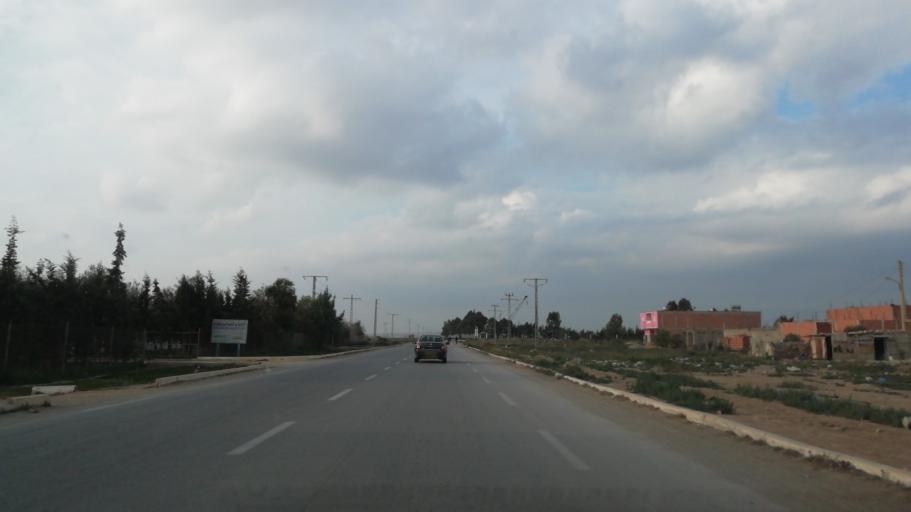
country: DZ
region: Mascara
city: Sig
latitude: 35.6923
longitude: -0.0190
